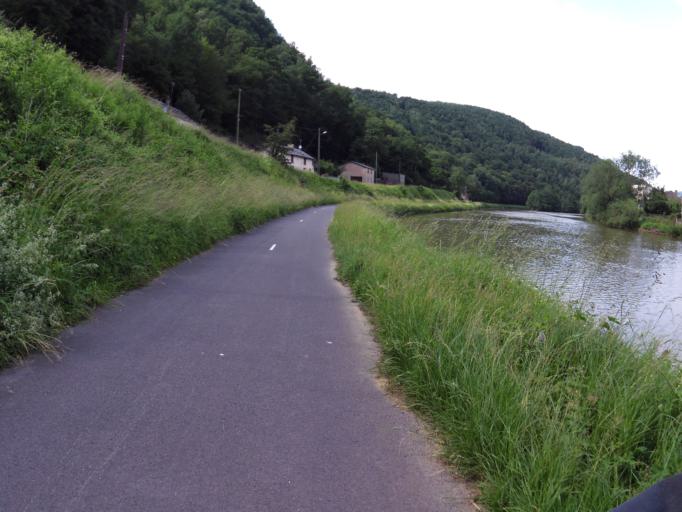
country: FR
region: Champagne-Ardenne
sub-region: Departement des Ardennes
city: Montherme
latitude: 49.8575
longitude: 4.7354
